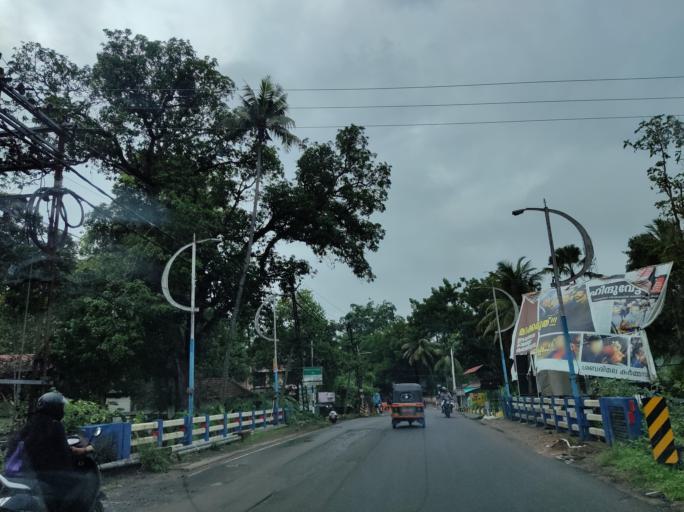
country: IN
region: Kerala
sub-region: Alappuzha
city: Mavelikara
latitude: 9.2499
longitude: 76.5331
